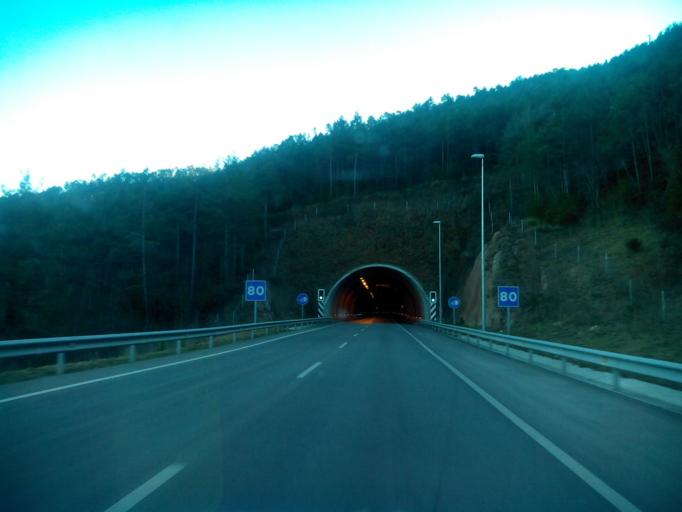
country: ES
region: Catalonia
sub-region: Provincia de Girona
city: Ripoll
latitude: 42.1629
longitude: 2.1971
